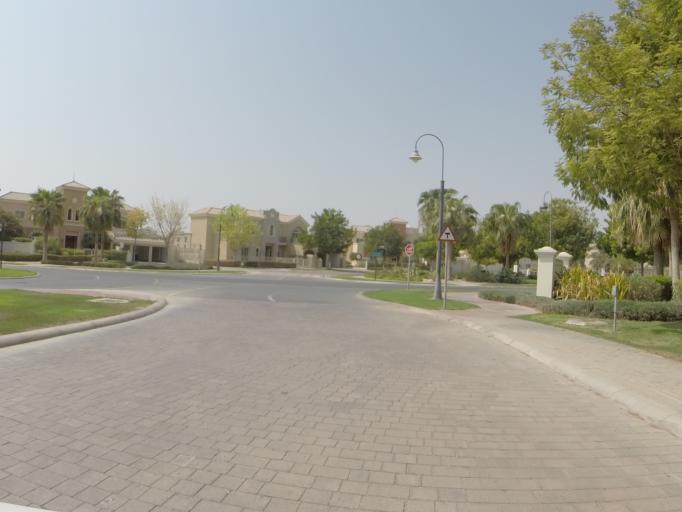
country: AE
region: Dubai
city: Dubai
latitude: 25.0372
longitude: 55.2143
